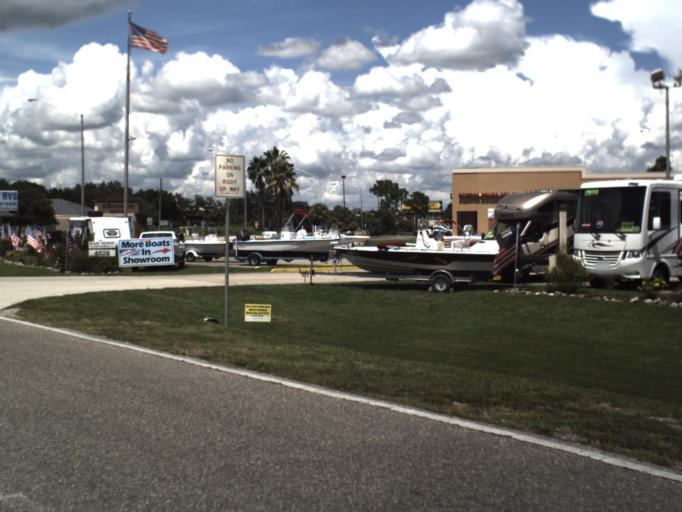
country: US
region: Florida
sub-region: Charlotte County
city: Charlotte Harbor
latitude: 26.9612
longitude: -82.0699
